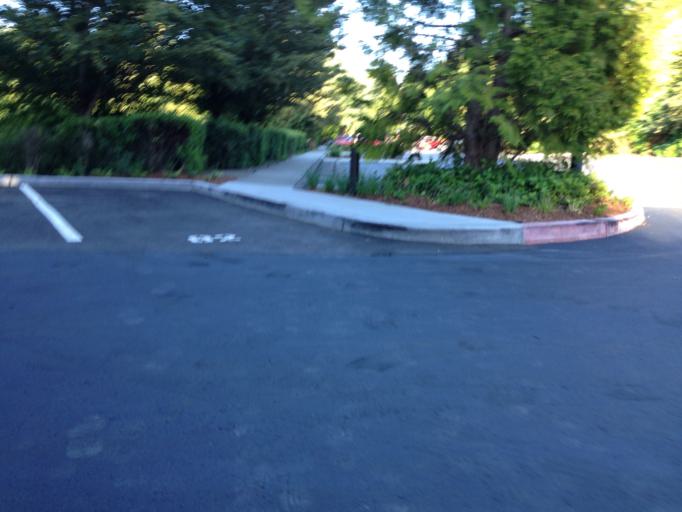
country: US
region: Washington
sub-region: King County
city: SeaTac
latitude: 47.4365
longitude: -122.2904
